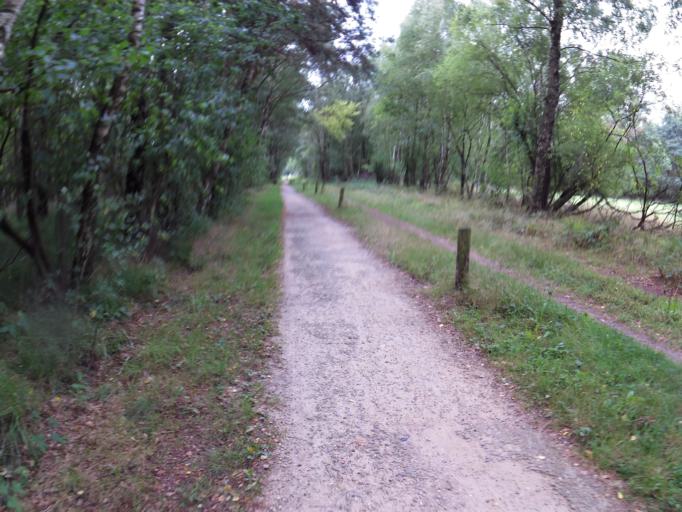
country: DE
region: North Rhine-Westphalia
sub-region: Regierungsbezirk Munster
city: Gronau
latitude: 52.2477
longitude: 7.1021
